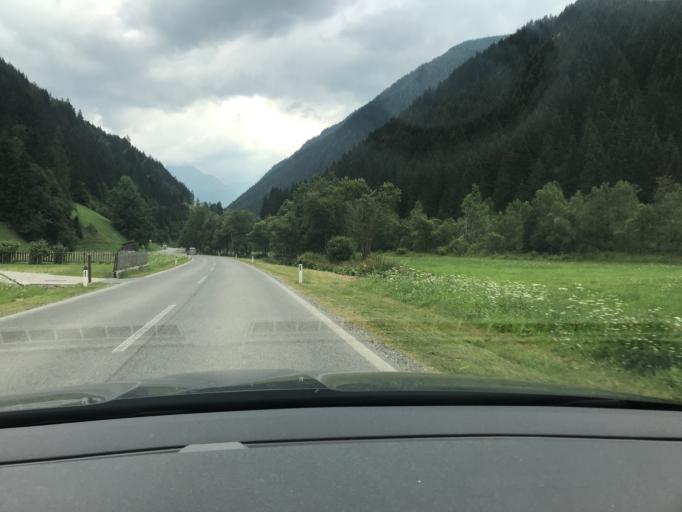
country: AT
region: Tyrol
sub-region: Politischer Bezirk Lienz
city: Hopfgarten in Defereggen
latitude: 46.9186
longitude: 12.4949
